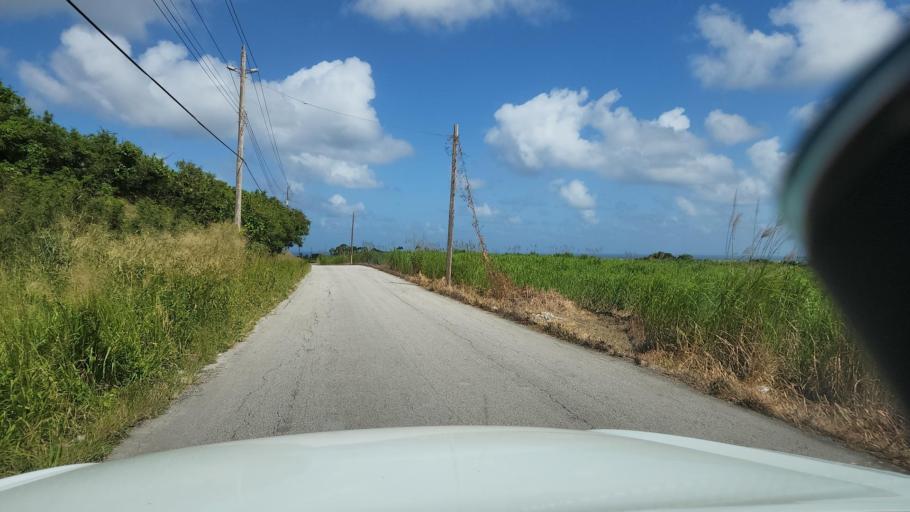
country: BB
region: Saint John
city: Four Cross Roads
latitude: 13.1521
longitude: -59.4692
